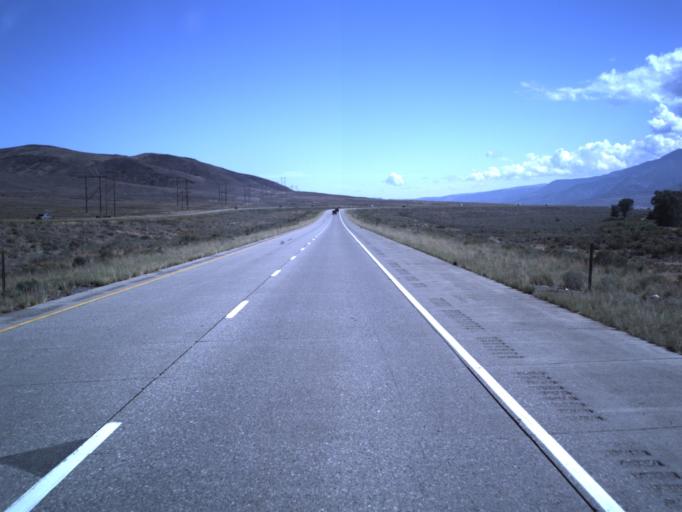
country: US
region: Utah
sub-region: Sevier County
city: Monroe
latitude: 38.6549
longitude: -112.2071
